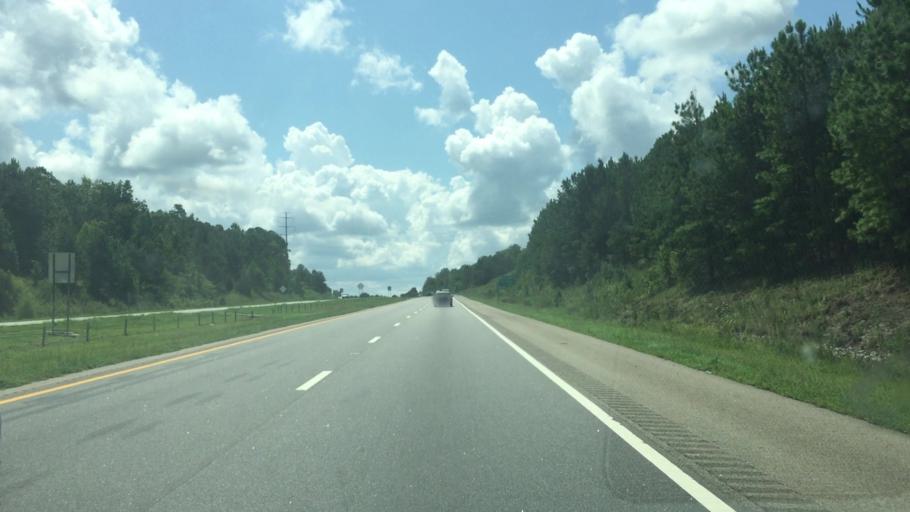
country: US
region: North Carolina
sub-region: Richmond County
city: Cordova
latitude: 34.9410
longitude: -79.8434
